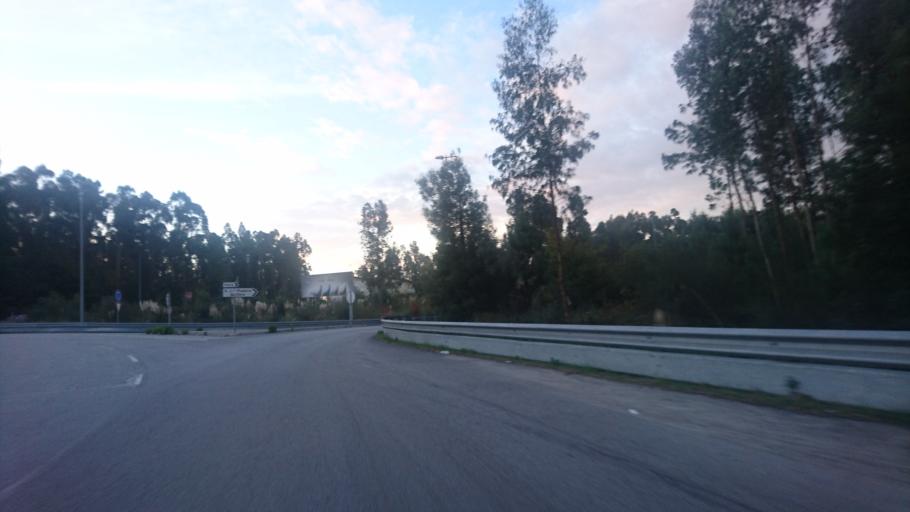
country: PT
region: Aveiro
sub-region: Santa Maria da Feira
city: Milheiros de Poiares
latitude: 40.9381
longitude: -8.4753
